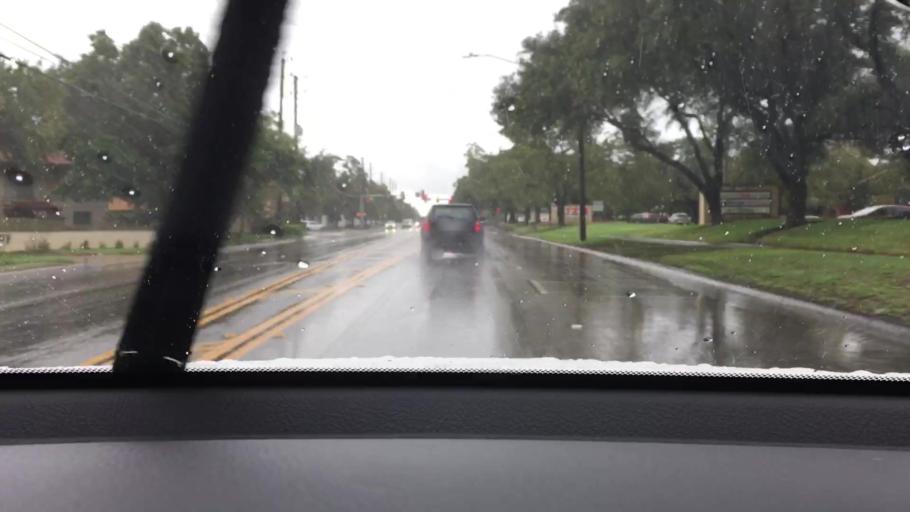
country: US
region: Texas
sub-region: Bexar County
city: Alamo Heights
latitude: 29.4989
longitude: -98.4666
